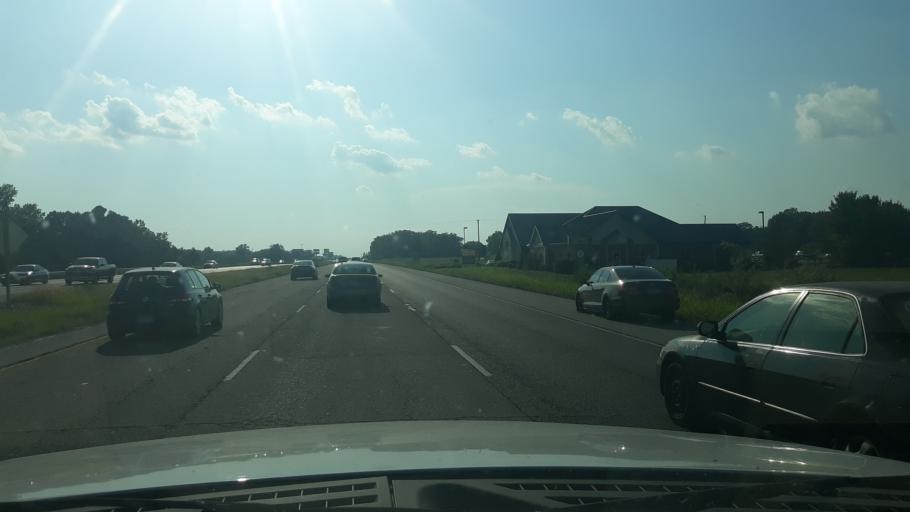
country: US
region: Illinois
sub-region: Williamson County
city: Energy
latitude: 37.7452
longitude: -89.0290
